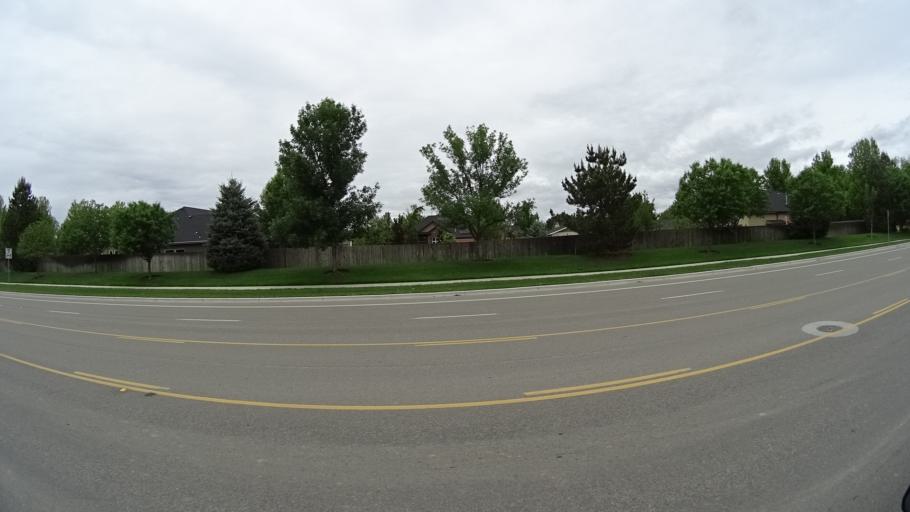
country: US
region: Idaho
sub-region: Ada County
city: Meridian
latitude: 43.6337
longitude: -116.3866
